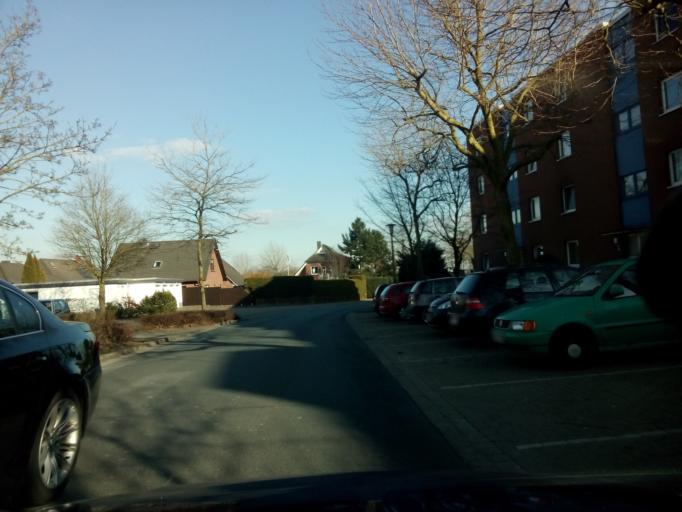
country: DE
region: Lower Saxony
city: Osterholz-Scharmbeck
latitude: 53.2382
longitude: 8.7928
